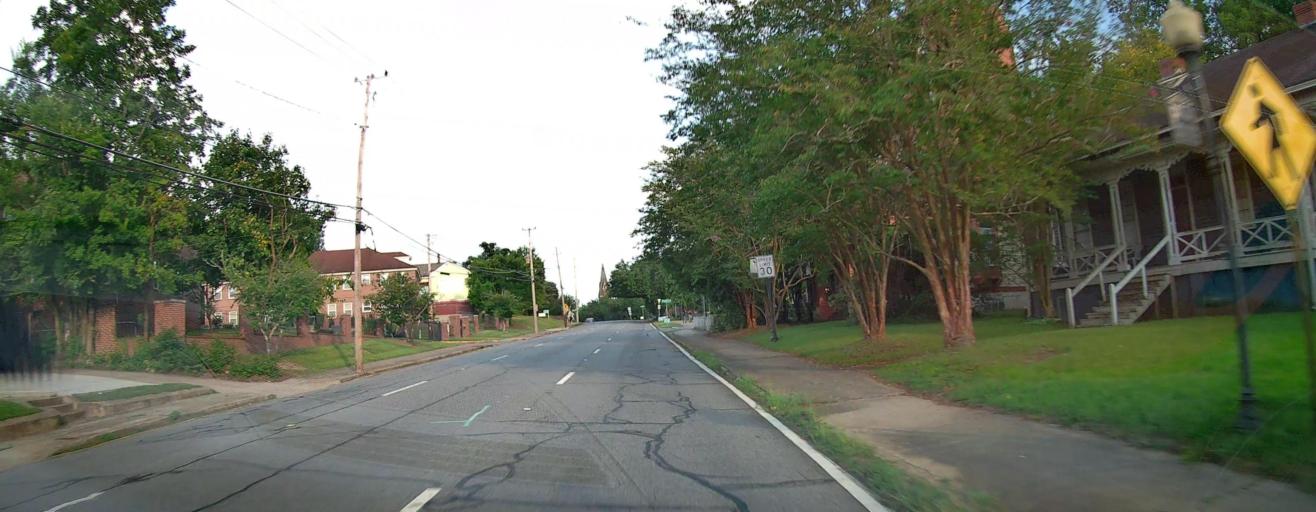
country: US
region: Georgia
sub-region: Bibb County
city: Macon
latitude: 32.8376
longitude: -83.6434
